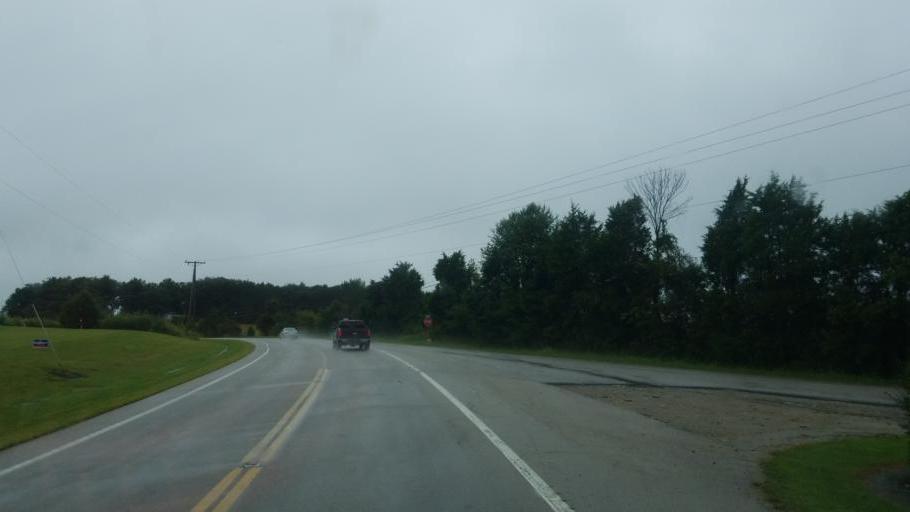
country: US
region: Ohio
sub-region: Adams County
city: West Union
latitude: 38.8011
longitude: -83.4731
